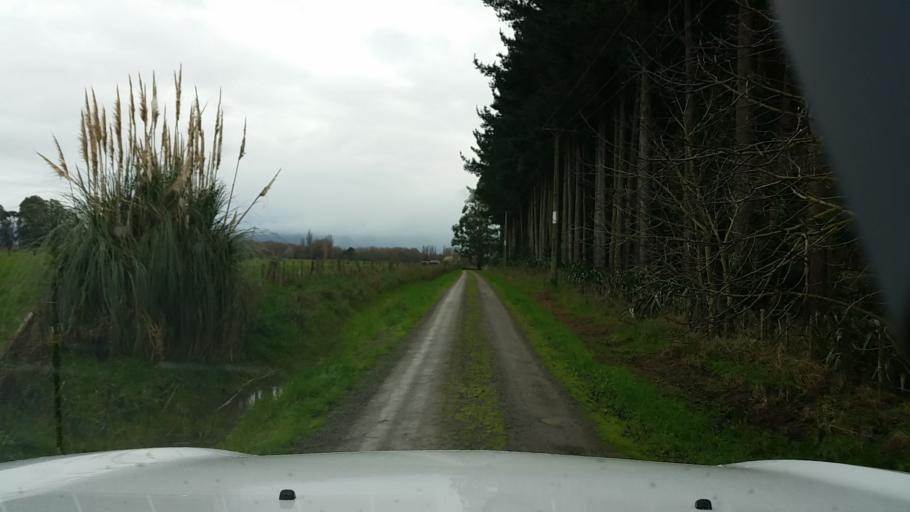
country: NZ
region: Wellington
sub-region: Masterton District
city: Masterton
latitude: -41.0964
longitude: 175.5197
